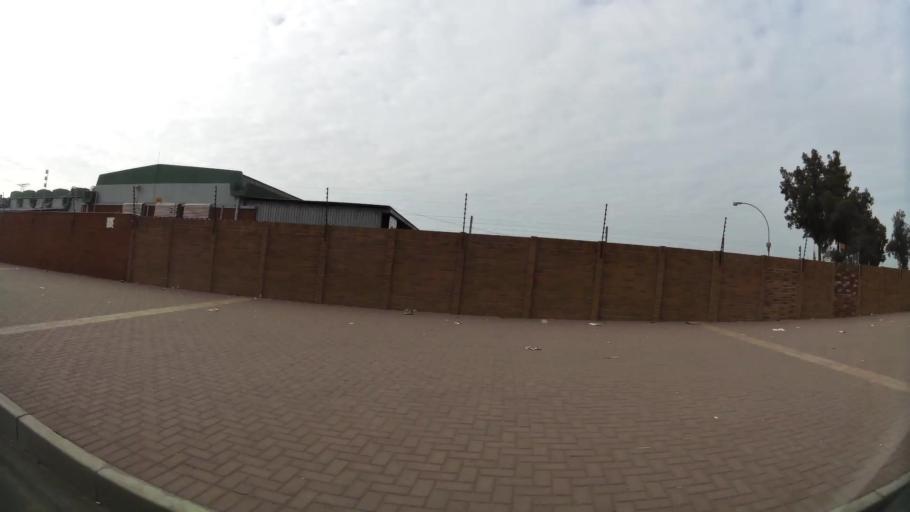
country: ZA
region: Orange Free State
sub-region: Mangaung Metropolitan Municipality
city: Bloemfontein
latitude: -29.1263
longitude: 26.2239
